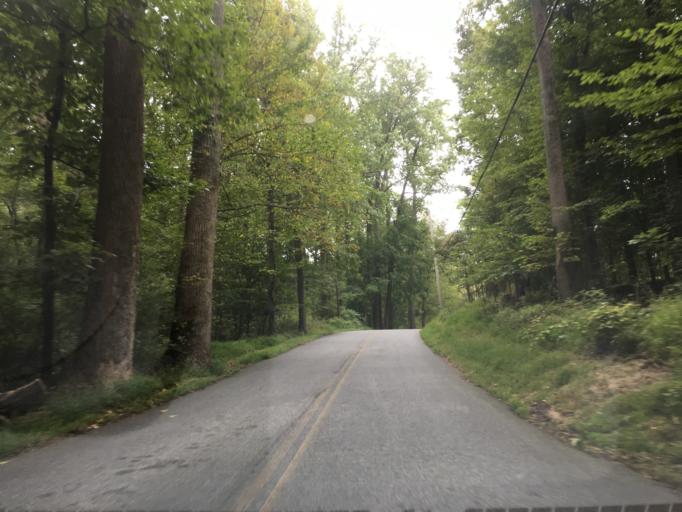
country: US
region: Maryland
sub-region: Baltimore County
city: Hunt Valley
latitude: 39.5102
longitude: -76.5829
